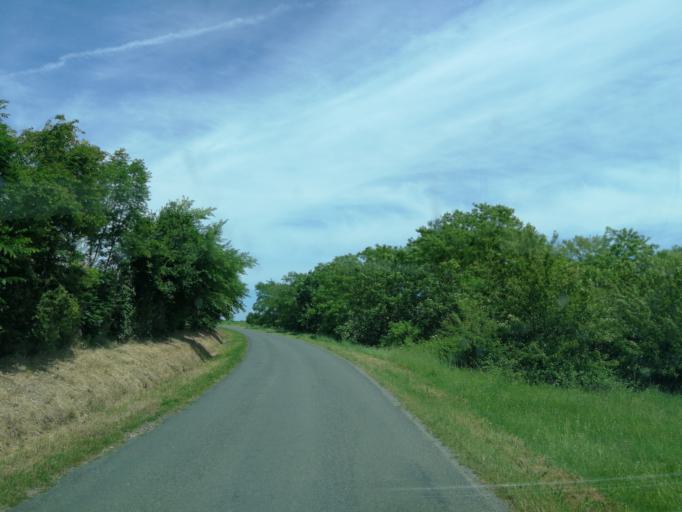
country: FR
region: Pays de la Loire
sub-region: Departement de la Vendee
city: Le Langon
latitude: 46.4276
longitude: -0.8916
